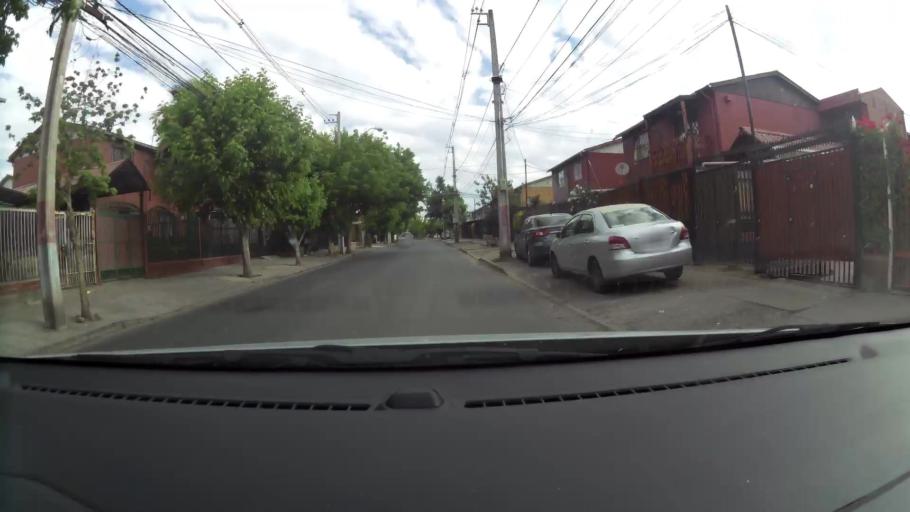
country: CL
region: Santiago Metropolitan
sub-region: Provincia de Cordillera
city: Puente Alto
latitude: -33.6249
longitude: -70.6075
